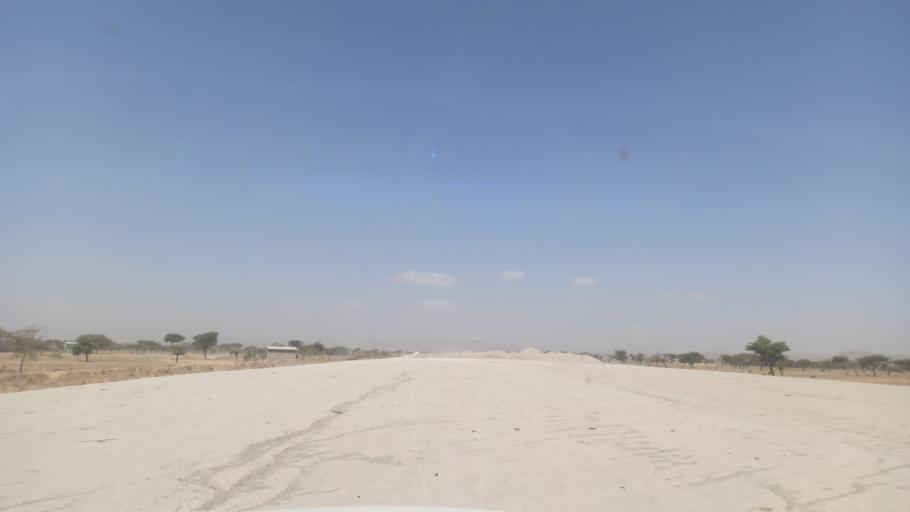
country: ET
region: Oromiya
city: Ziway
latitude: 7.7202
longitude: 38.6311
